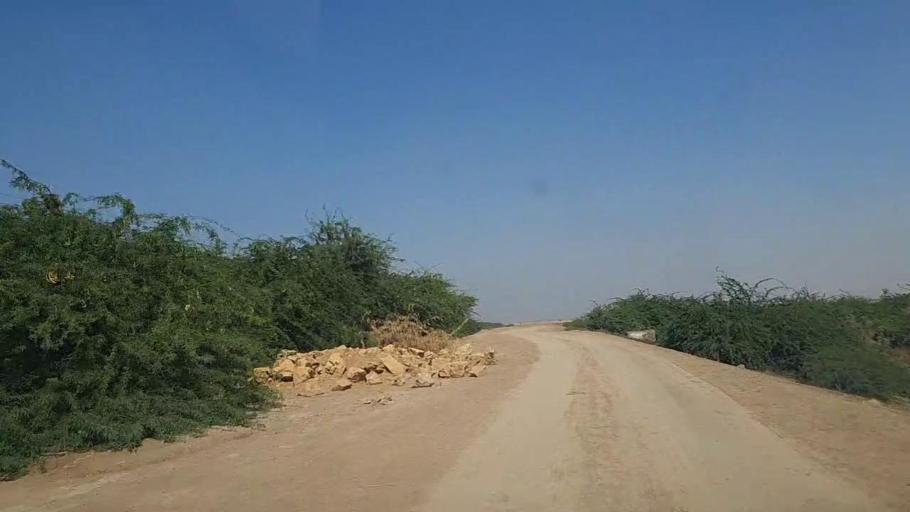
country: PK
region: Sindh
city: Daro Mehar
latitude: 24.9055
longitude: 68.0758
